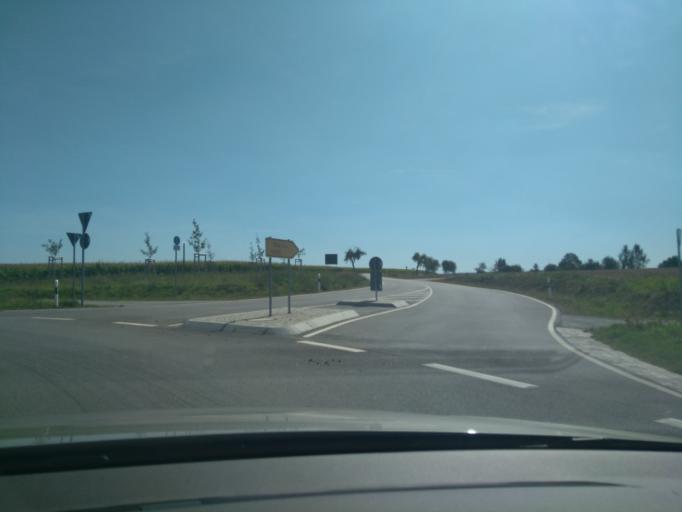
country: DE
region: Saxony
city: Goda
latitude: 51.1972
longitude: 14.3237
